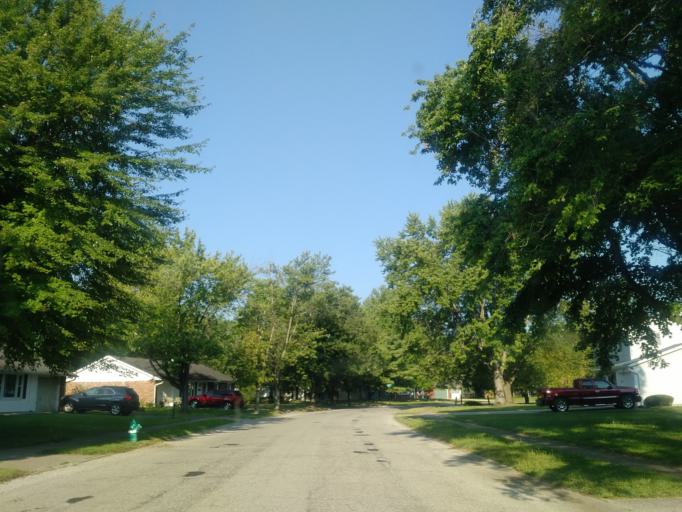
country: US
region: Indiana
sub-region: Marion County
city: Cumberland
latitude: 39.7928
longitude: -85.9861
